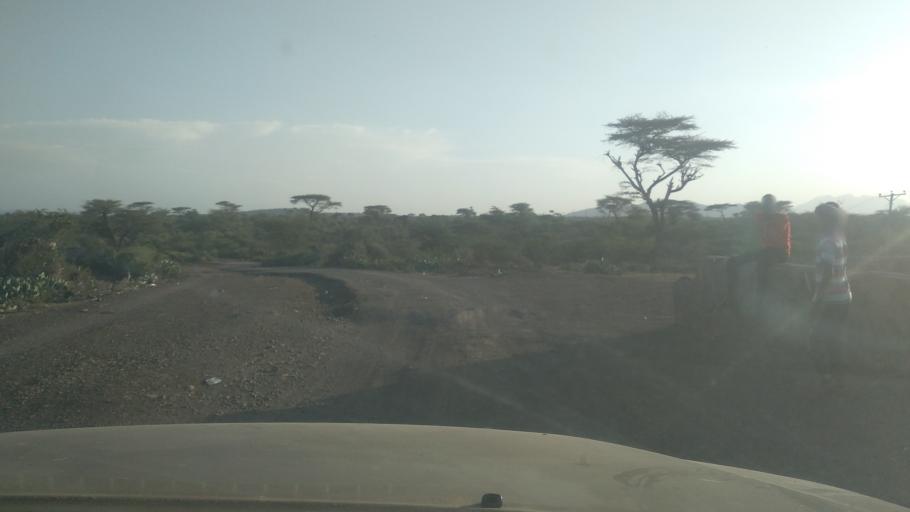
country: ET
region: Oromiya
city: Asbe Teferi
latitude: 9.2899
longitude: 40.8321
